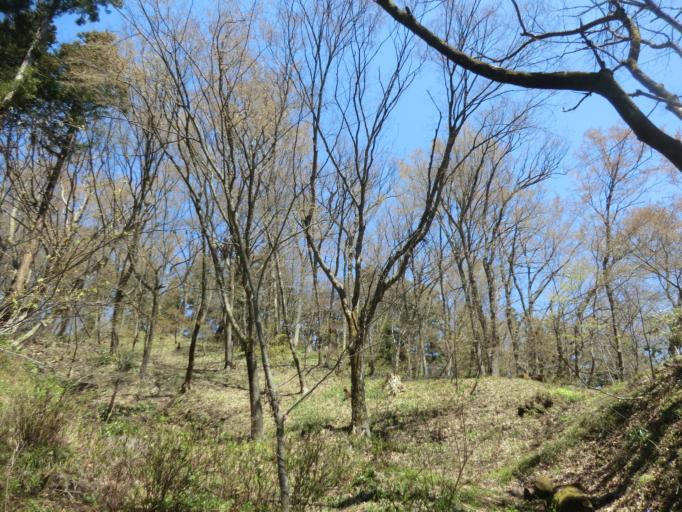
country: JP
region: Niigata
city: Nagaoka
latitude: 37.4656
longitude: 138.7437
